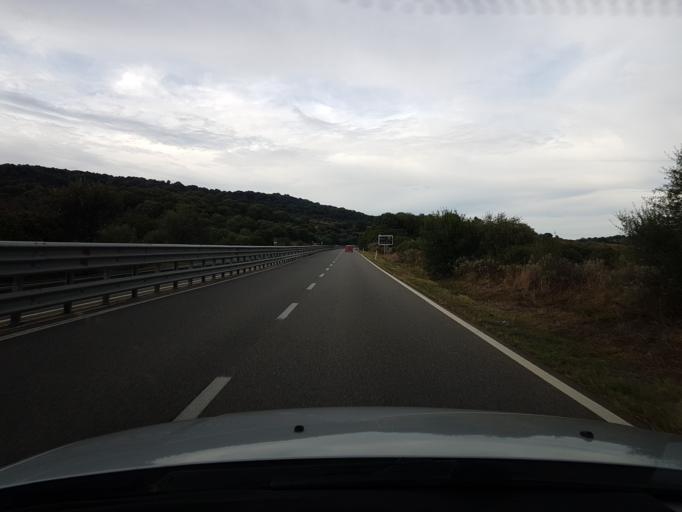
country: IT
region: Sardinia
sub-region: Provincia di Oristano
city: Sedilo
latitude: 40.1551
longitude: 8.9044
